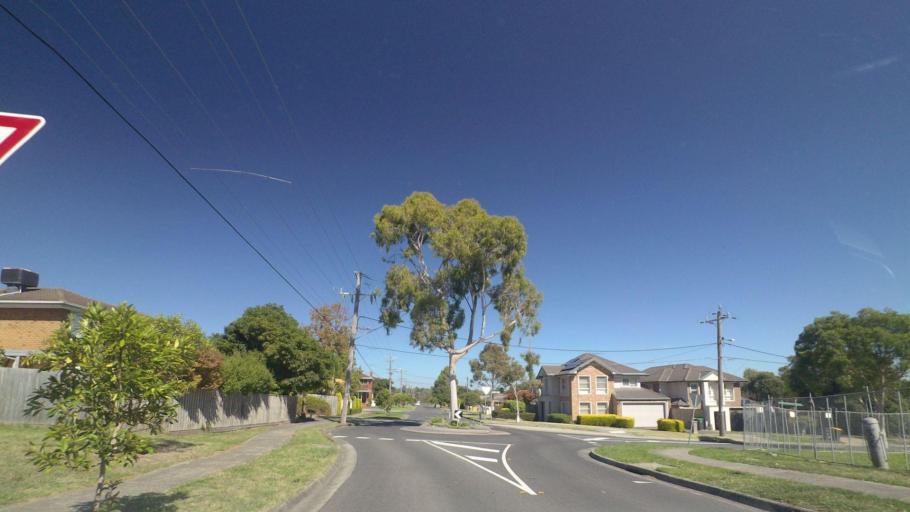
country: AU
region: Victoria
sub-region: Manningham
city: Donvale
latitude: -37.7966
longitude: 145.1698
